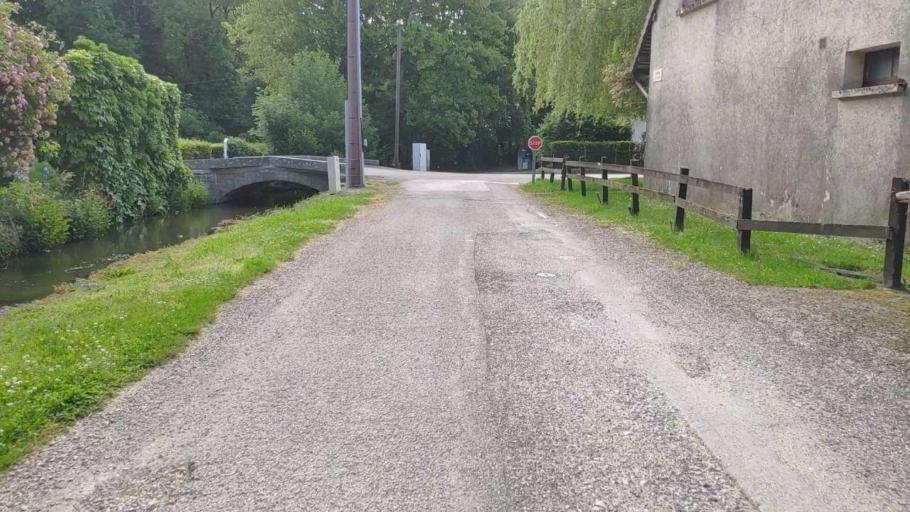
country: FR
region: Franche-Comte
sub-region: Departement du Jura
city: Bletterans
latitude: 46.7352
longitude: 5.4628
